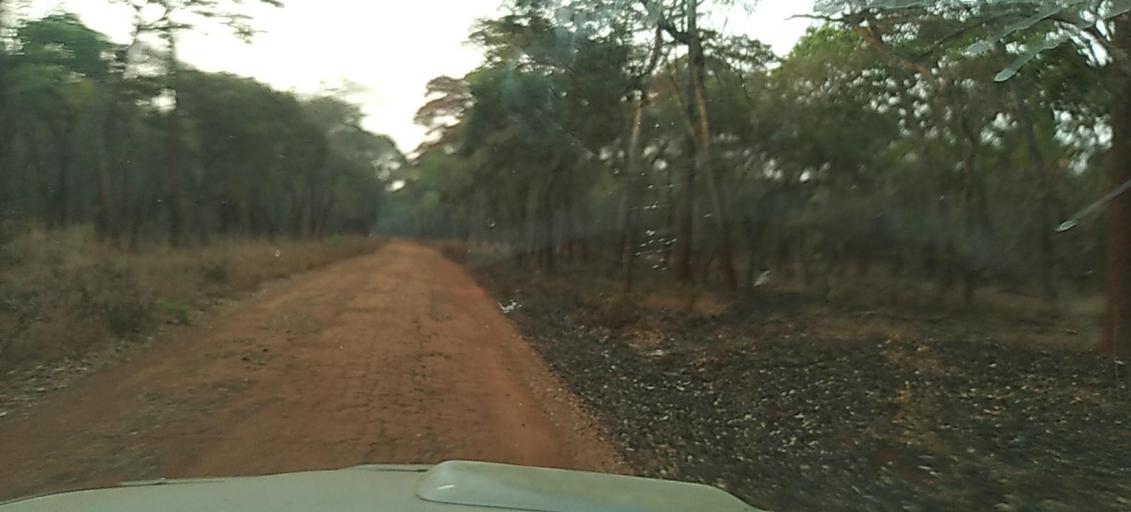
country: ZM
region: North-Western
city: Kasempa
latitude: -13.0953
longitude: 26.4014
